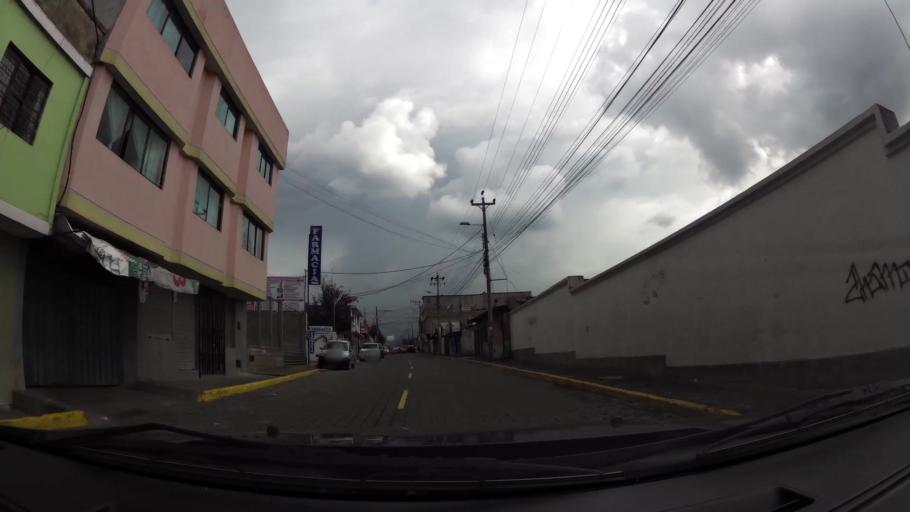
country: EC
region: Pichincha
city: Sangolqui
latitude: -0.3383
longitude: -78.4531
